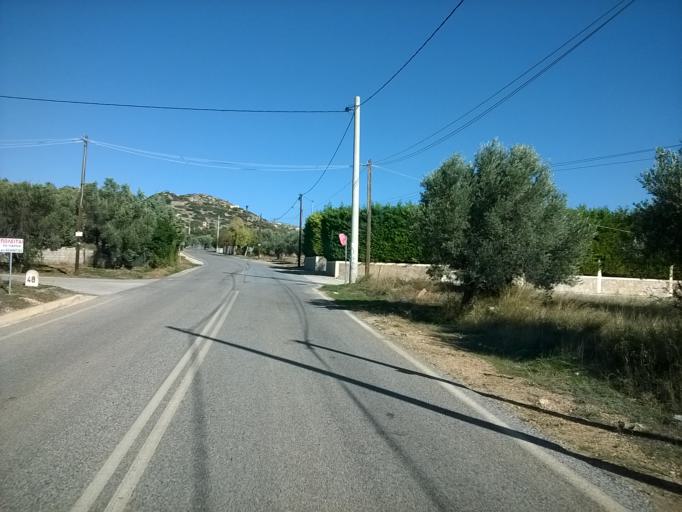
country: GR
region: Attica
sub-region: Nomarchia Anatolikis Attikis
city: Keratea
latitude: 37.7633
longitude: 23.9812
